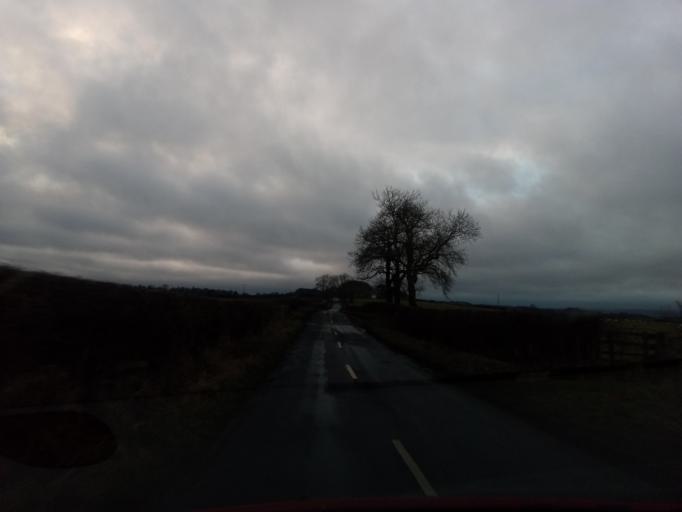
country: GB
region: England
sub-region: Northumberland
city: Meldon
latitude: 55.1419
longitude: -1.8220
